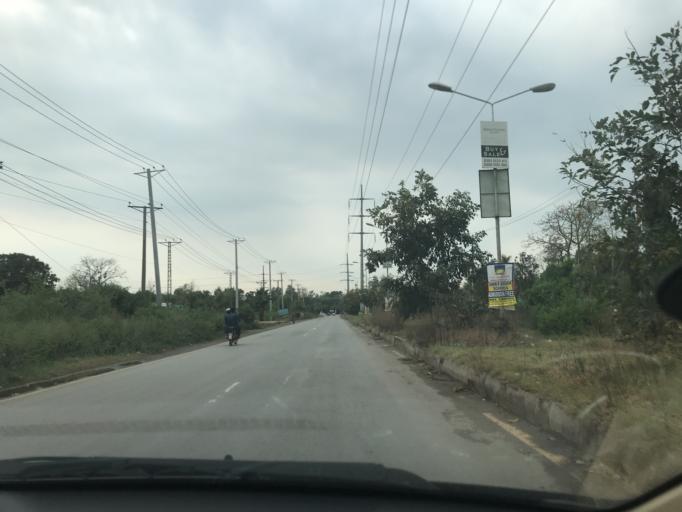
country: PK
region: Punjab
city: Rawalpindi
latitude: 33.6761
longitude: 73.1472
